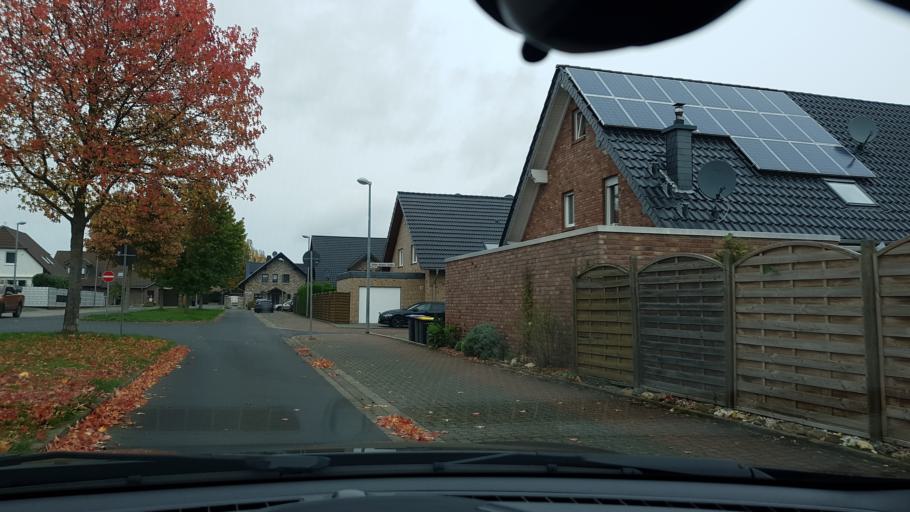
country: DE
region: North Rhine-Westphalia
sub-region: Regierungsbezirk Koln
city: Bedburg
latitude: 51.0002
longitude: 6.5513
